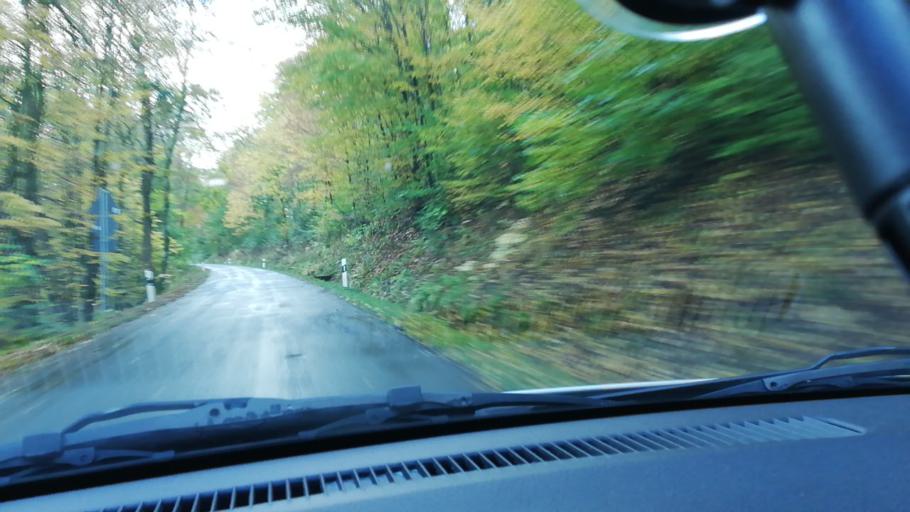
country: DE
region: Bavaria
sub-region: Regierungsbezirk Unterfranken
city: Bischbrunn
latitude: 49.9194
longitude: 9.5041
